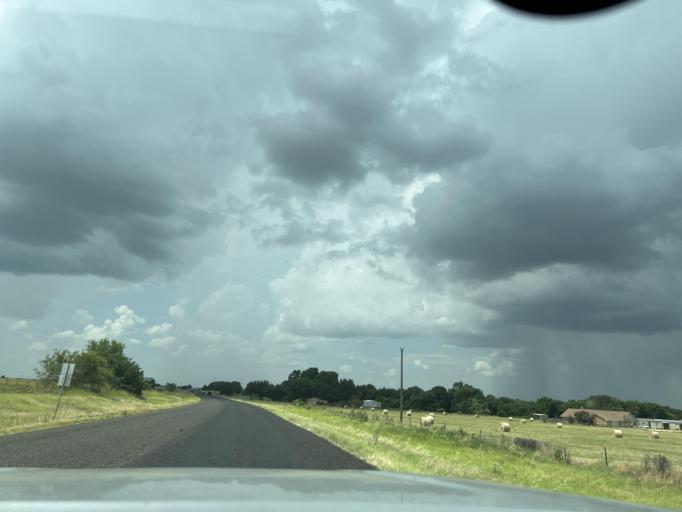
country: US
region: Texas
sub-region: Wise County
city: Decatur
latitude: 33.1856
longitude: -97.6171
